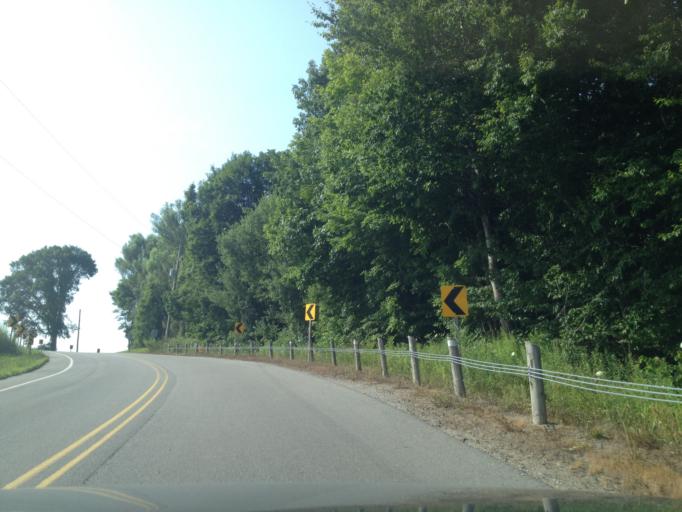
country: CA
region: Ontario
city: Aylmer
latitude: 42.7577
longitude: -80.8450
